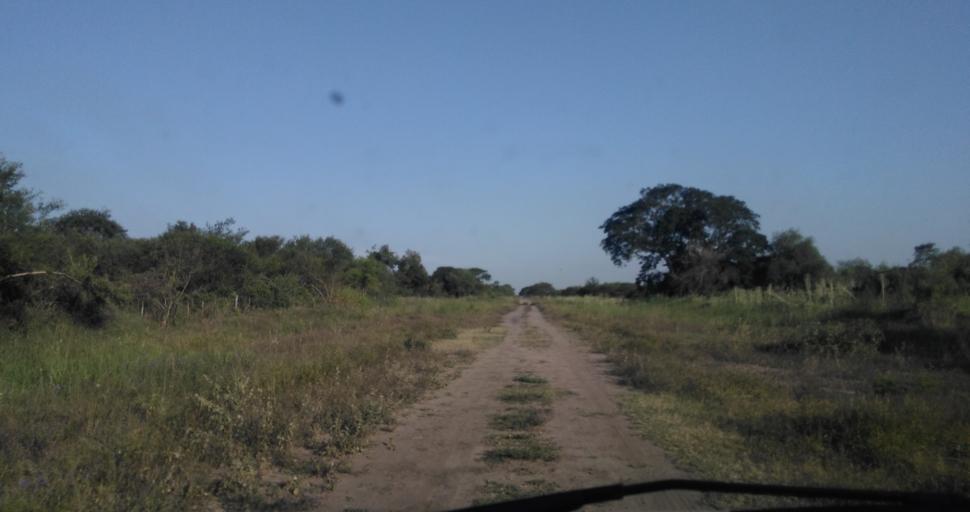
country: AR
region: Chaco
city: Fontana
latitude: -27.4274
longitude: -59.0549
